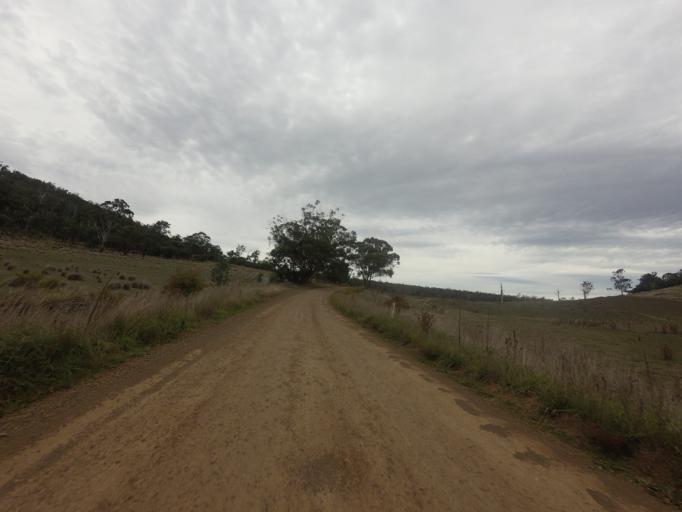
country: AU
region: Tasmania
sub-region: Derwent Valley
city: New Norfolk
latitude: -42.5634
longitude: 146.9286
